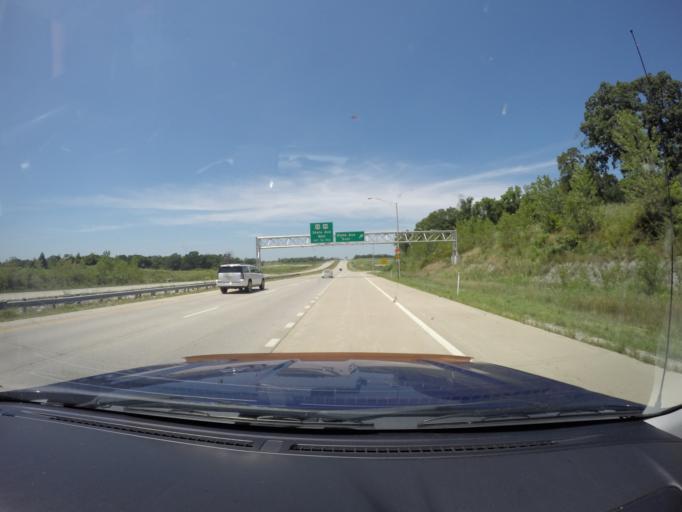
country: US
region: Kansas
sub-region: Wyandotte County
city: Bonner Springs
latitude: 39.1119
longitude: -94.8902
